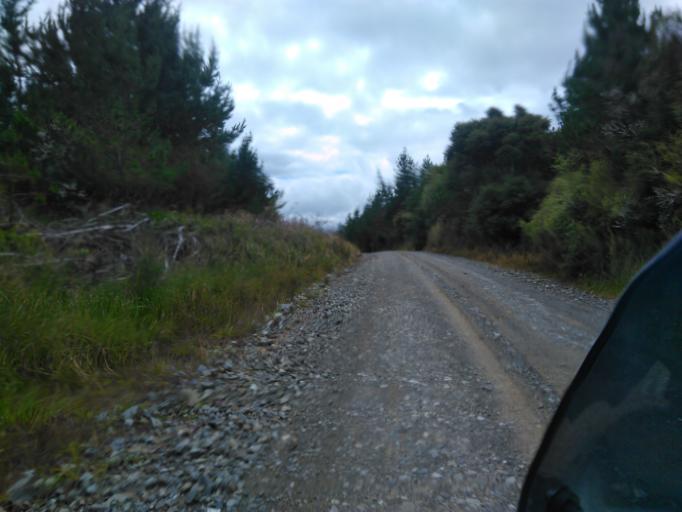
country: NZ
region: Gisborne
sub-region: Gisborne District
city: Gisborne
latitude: -38.1842
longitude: 178.1157
